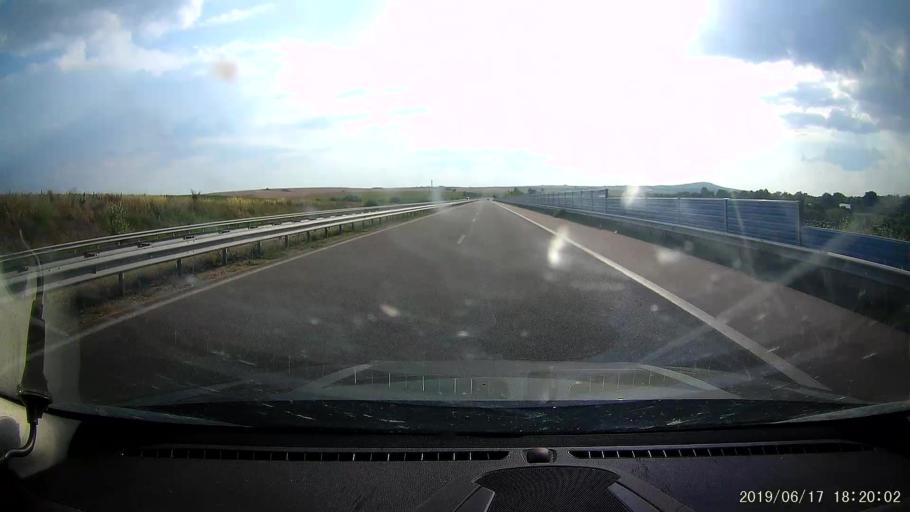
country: BG
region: Khaskovo
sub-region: Obshtina Simeonovgrad
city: Simeonovgrad
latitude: 41.9626
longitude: 25.8267
